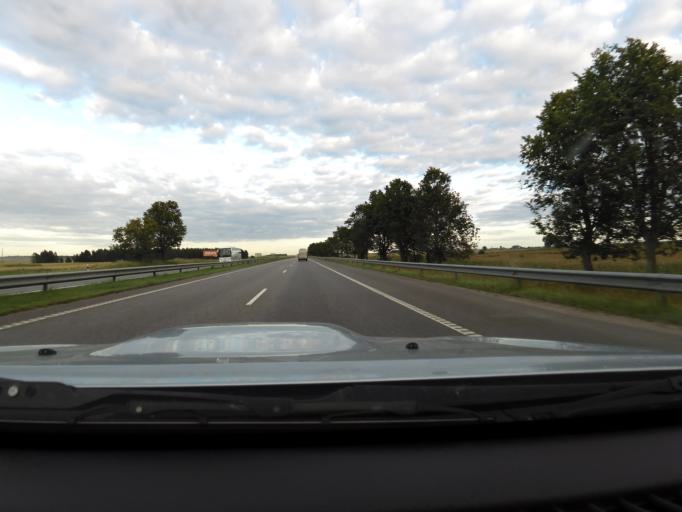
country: LT
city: Kaisiadorys
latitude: 54.8597
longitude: 24.2738
